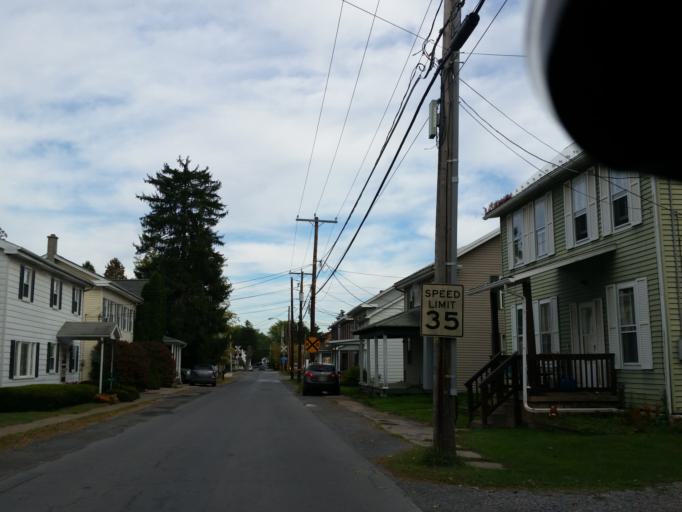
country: US
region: Pennsylvania
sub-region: Union County
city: New Columbia
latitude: 41.0406
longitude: -76.8666
